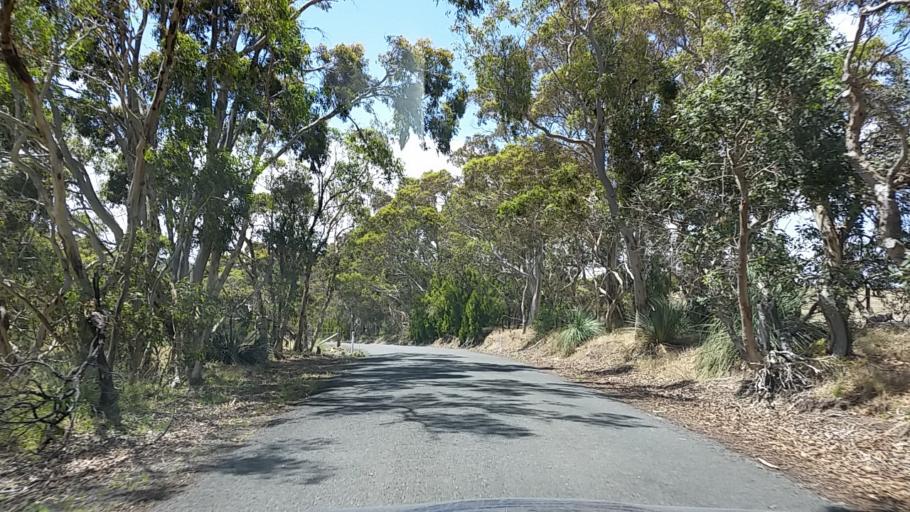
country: AU
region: South Australia
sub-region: Alexandrina
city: Mount Compass
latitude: -35.4455
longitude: 138.5927
